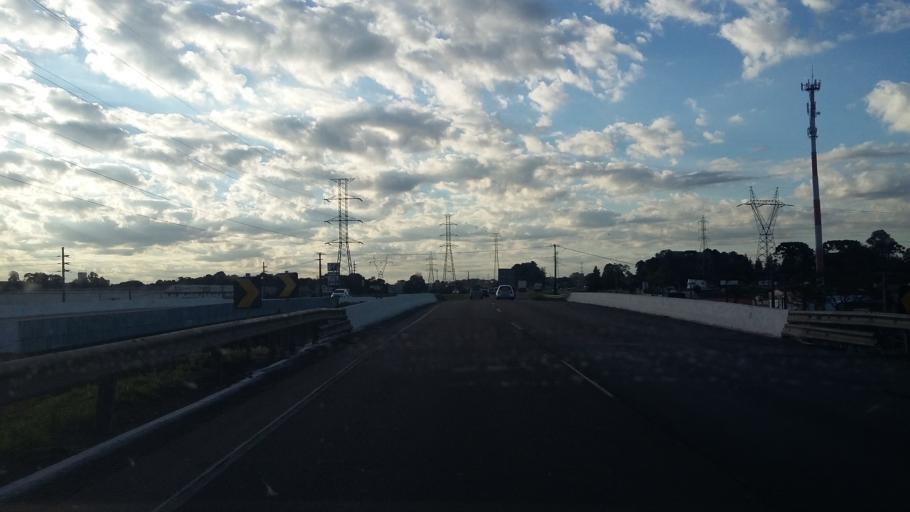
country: BR
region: Parana
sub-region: Curitiba
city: Curitiba
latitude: -25.4521
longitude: -49.3622
